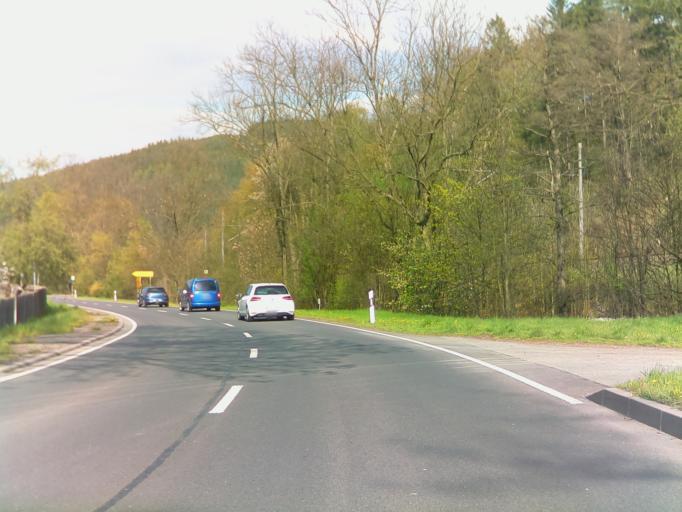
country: DE
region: Thuringia
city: Probstzella
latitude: 50.5833
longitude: 11.4040
